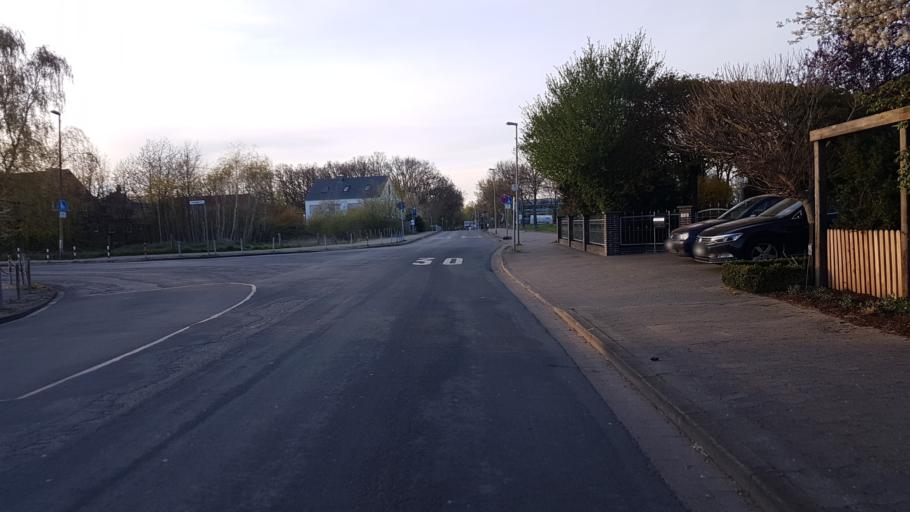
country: DE
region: Lower Saxony
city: Isernhagen Farster Bauerschaft
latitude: 52.4370
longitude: 9.8554
